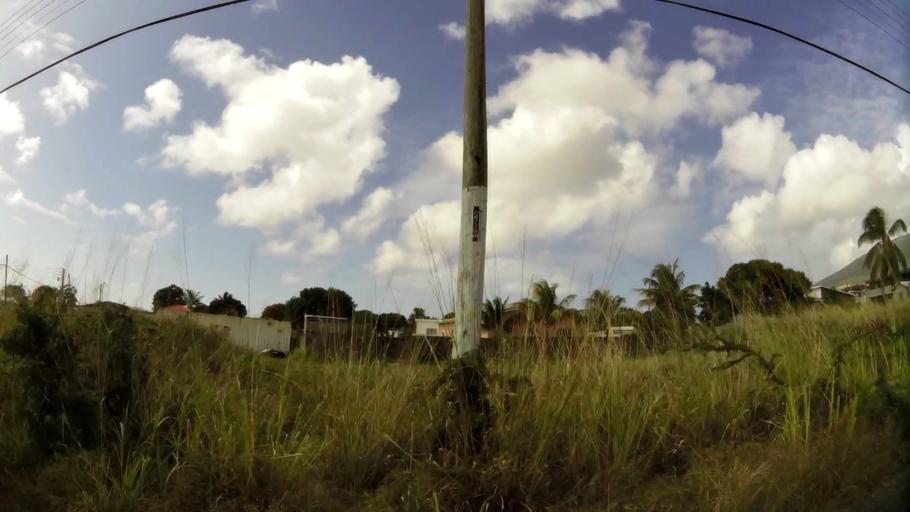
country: KN
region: Saint George Basseterre
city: Basseterre
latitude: 17.3019
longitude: -62.7281
